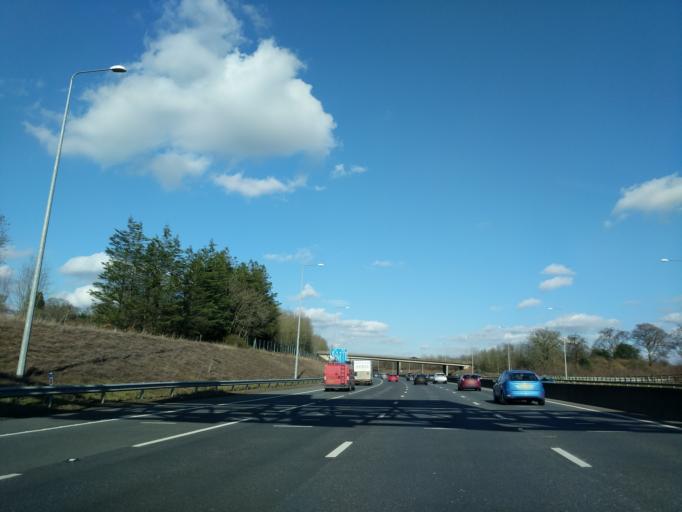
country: GB
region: England
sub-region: Hertfordshire
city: Kings Langley
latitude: 51.6834
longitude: -0.4490
